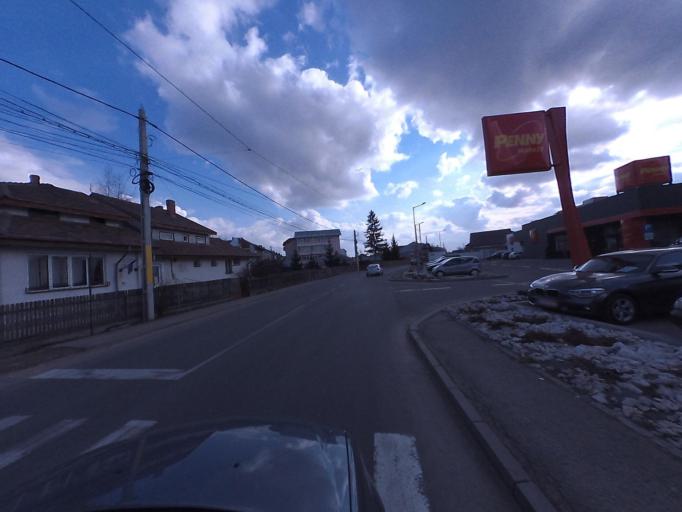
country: RO
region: Neamt
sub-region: Oras Targu Neamt
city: Targu Neamt
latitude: 47.2055
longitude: 26.3734
